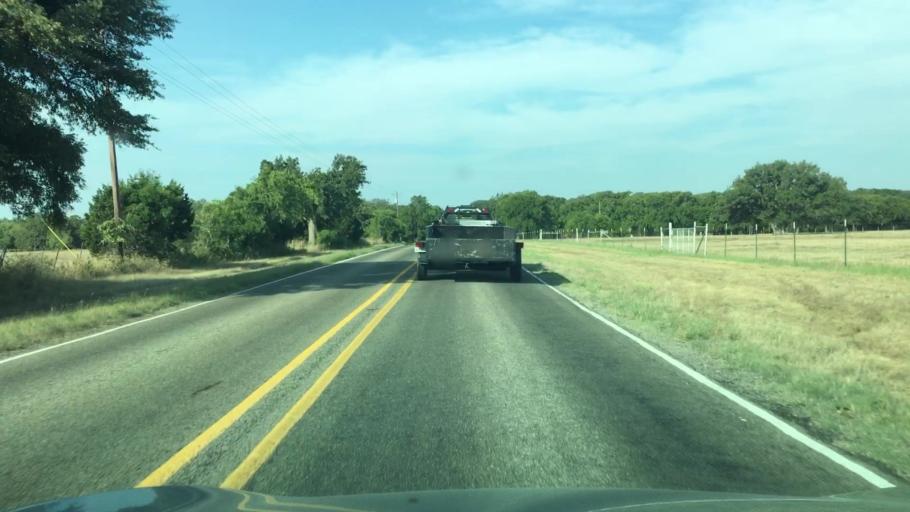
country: US
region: Texas
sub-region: Hays County
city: Dripping Springs
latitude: 30.1860
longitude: -98.2179
